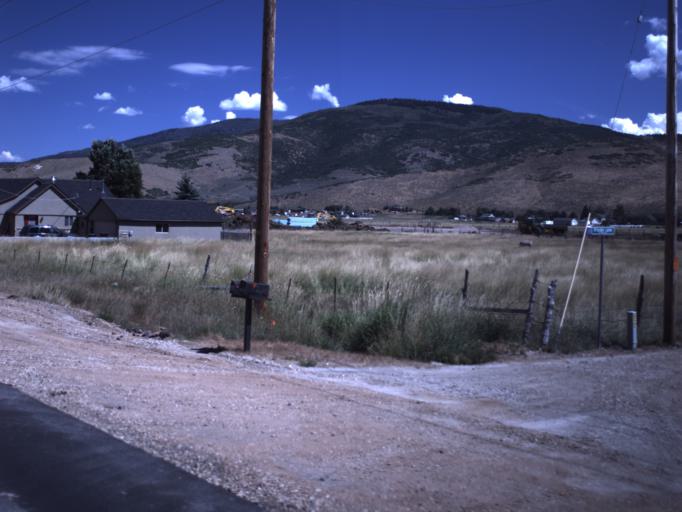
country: US
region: Utah
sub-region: Summit County
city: Francis
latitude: 40.6214
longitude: -111.2807
